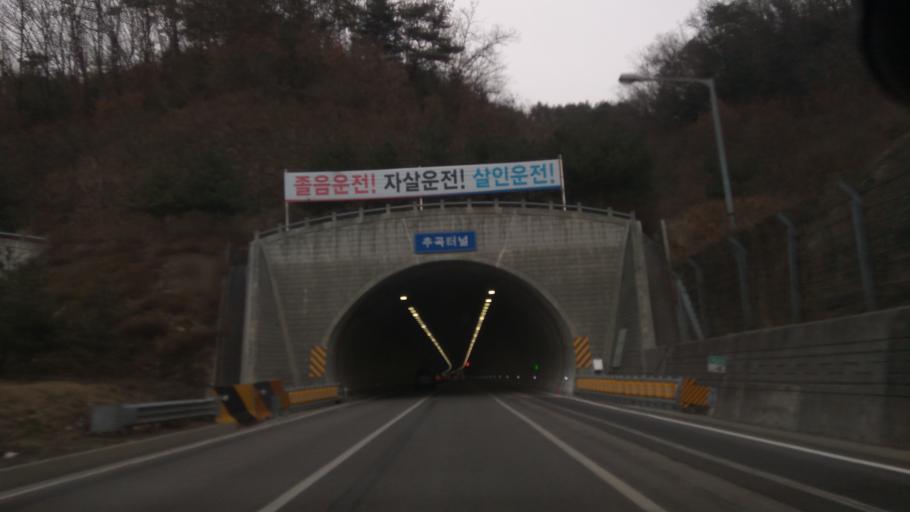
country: KR
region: Gangwon-do
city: Sindong
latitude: 37.7404
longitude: 127.6588
